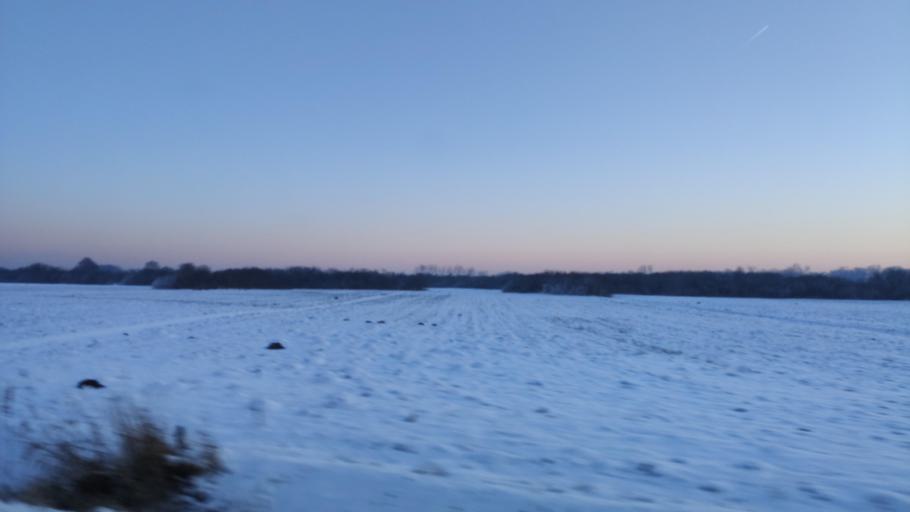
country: PL
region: Kujawsko-Pomorskie
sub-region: Powiat zninski
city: Barcin
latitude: 52.8755
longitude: 17.8662
